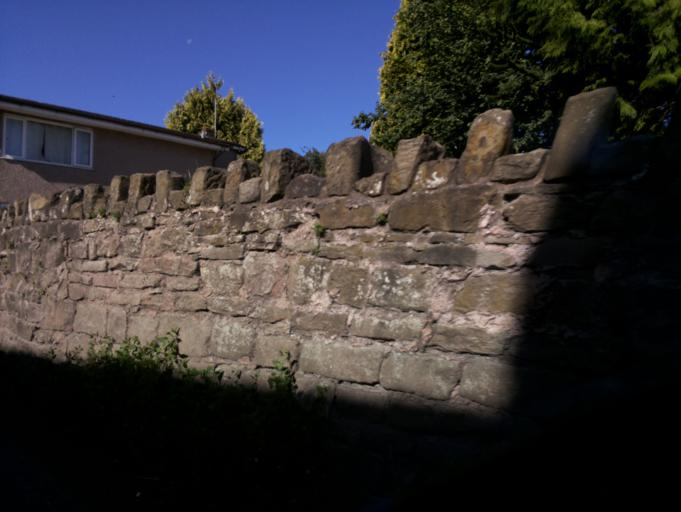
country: GB
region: England
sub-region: Gloucestershire
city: Coleford
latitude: 51.8184
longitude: -2.6221
